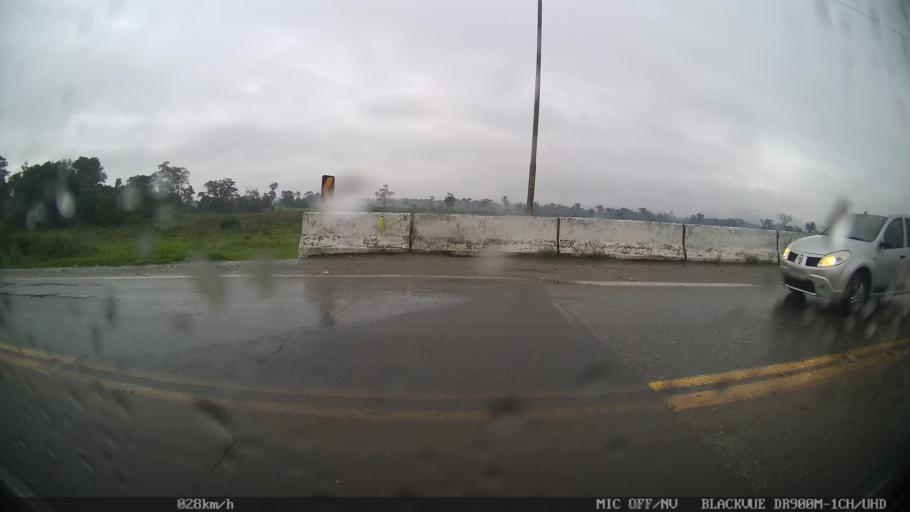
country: BR
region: Santa Catarina
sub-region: Itajai
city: Itajai
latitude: -26.9190
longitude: -48.7109
